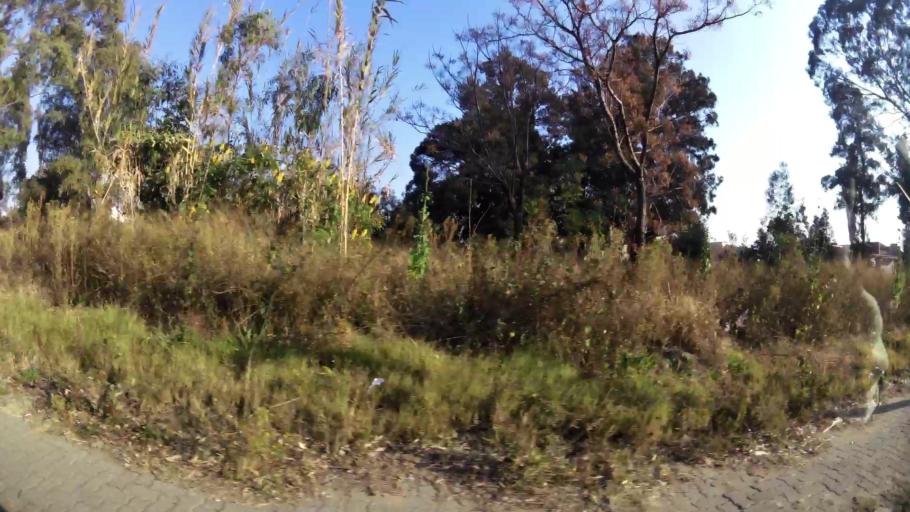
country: ZA
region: Gauteng
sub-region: City of Johannesburg Metropolitan Municipality
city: Modderfontein
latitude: -26.0903
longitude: 28.1018
